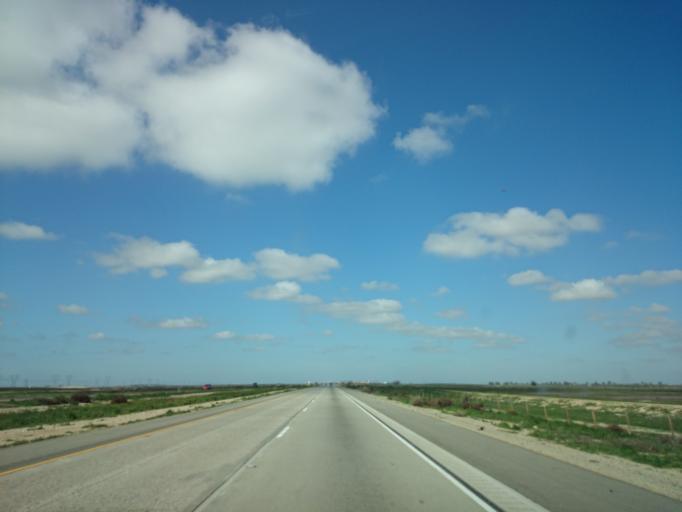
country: US
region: California
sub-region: Kern County
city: Rosedale
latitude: 35.3347
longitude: -119.3072
